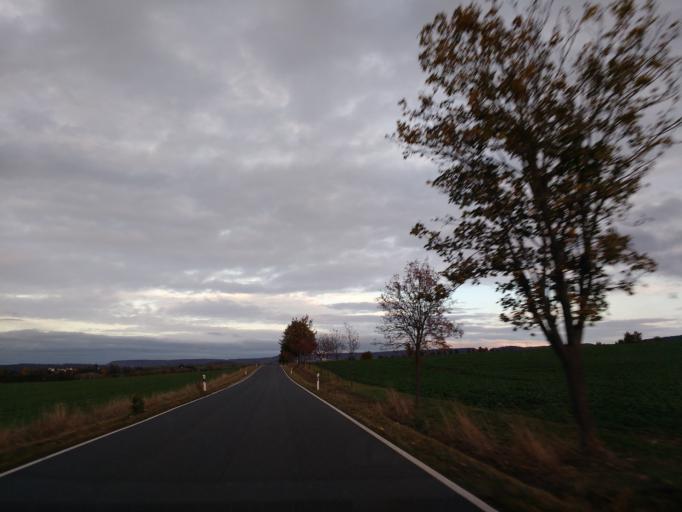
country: DE
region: Thuringia
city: Niederorschel
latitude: 51.3578
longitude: 10.4094
